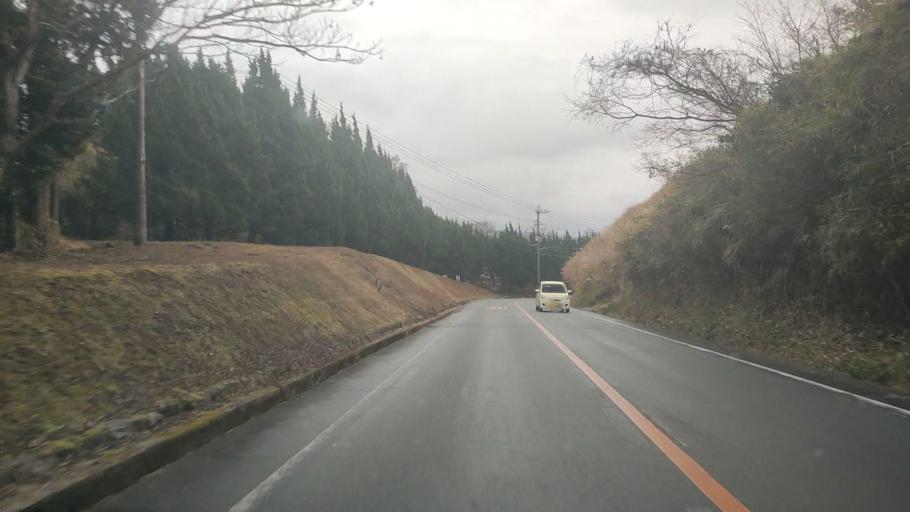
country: JP
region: Kumamoto
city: Aso
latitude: 32.8962
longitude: 130.9995
